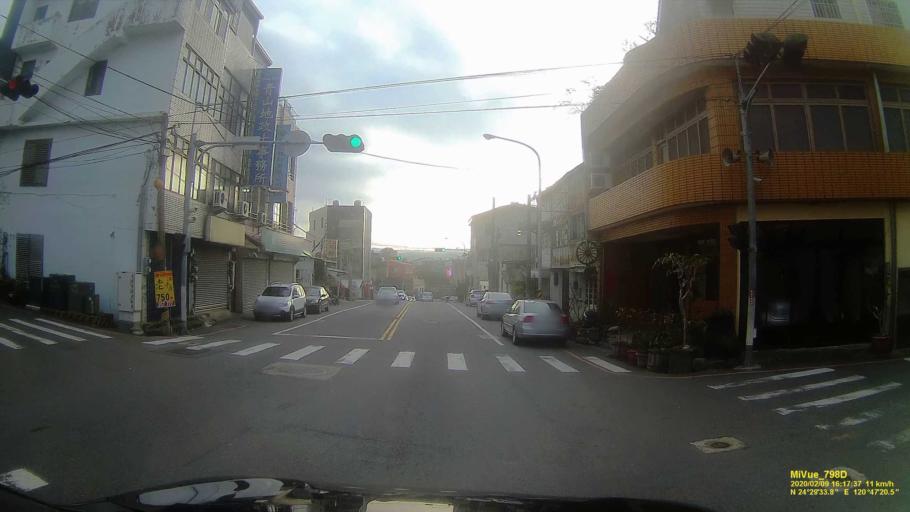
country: TW
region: Taiwan
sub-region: Miaoli
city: Miaoli
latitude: 24.4927
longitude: 120.7890
